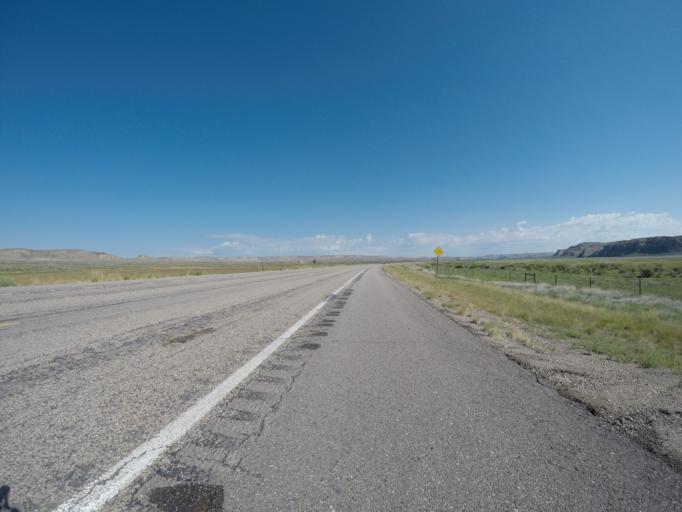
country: US
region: Wyoming
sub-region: Sublette County
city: Marbleton
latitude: 42.1276
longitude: -110.1884
